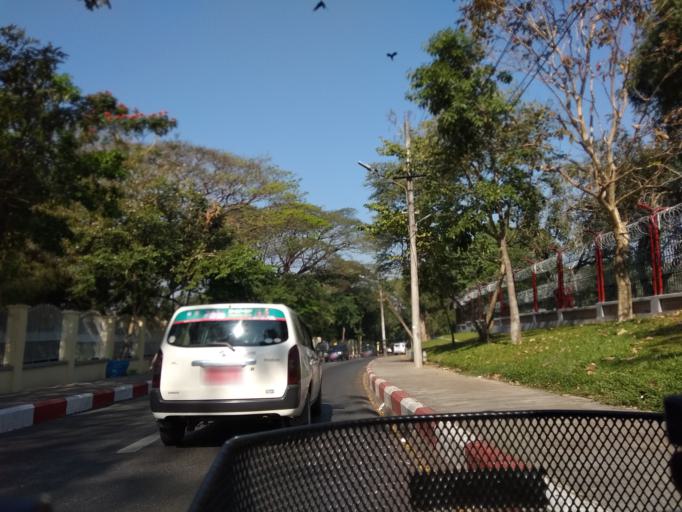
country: MM
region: Yangon
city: Yangon
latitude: 16.8017
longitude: 96.1480
